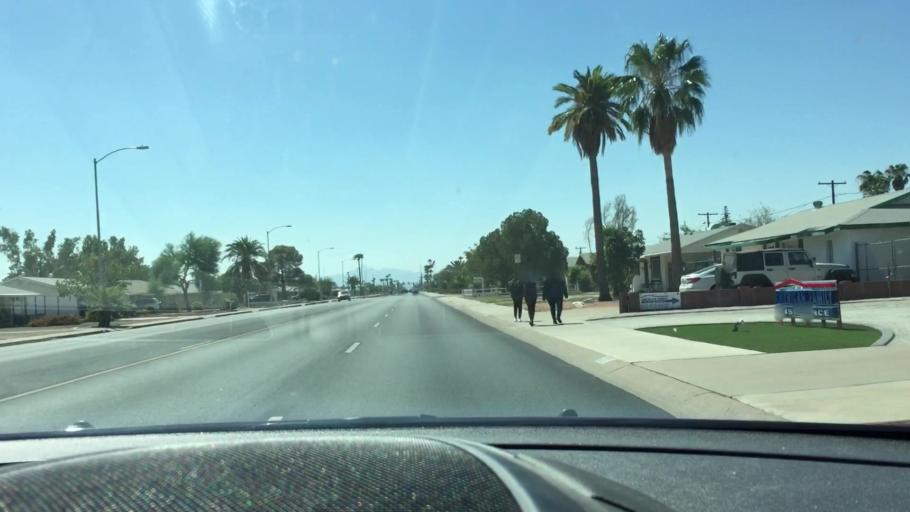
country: US
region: Arizona
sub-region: Maricopa County
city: Youngtown
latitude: 33.6006
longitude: -112.2988
